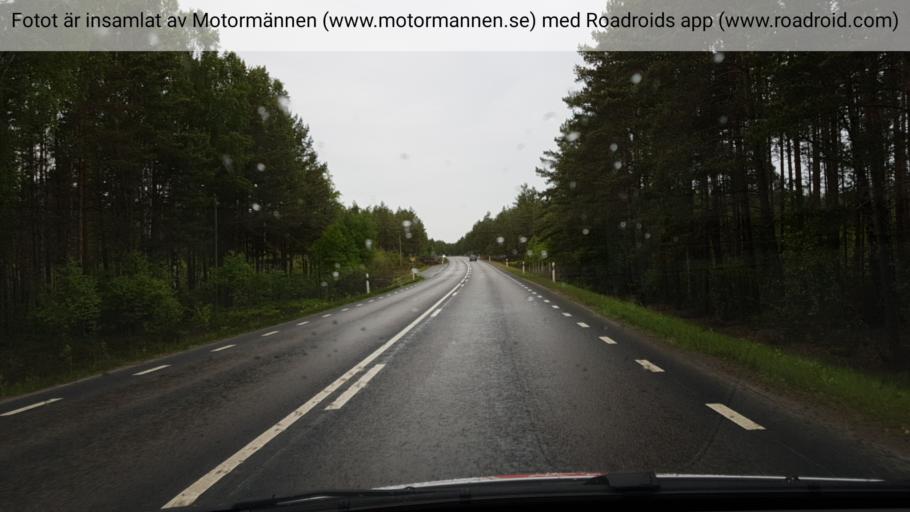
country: SE
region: Kalmar
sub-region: Hultsfreds Kommun
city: Malilla
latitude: 57.3958
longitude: 15.8076
